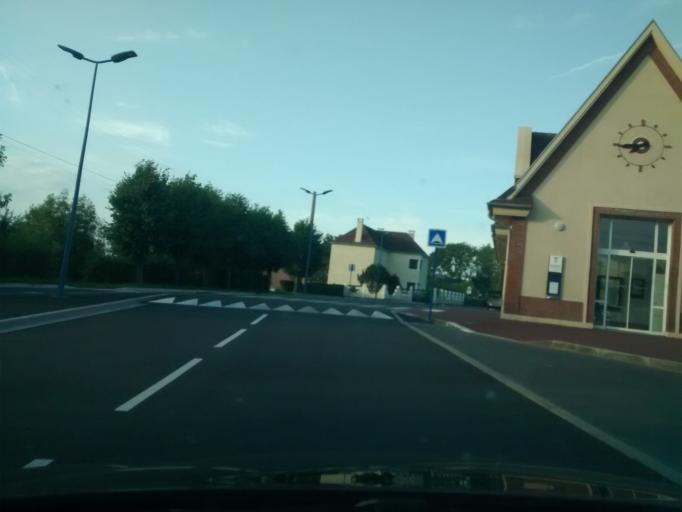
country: FR
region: Lower Normandy
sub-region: Departement du Calvados
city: Villers-sur-Mer
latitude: 49.3158
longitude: 0.0094
